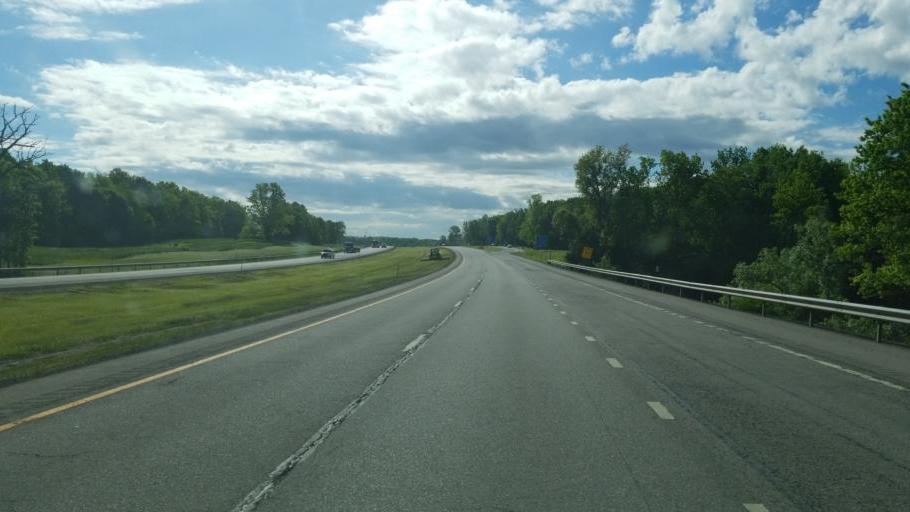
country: US
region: New York
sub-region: Monroe County
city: Pittsford
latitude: 43.0165
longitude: -77.4850
